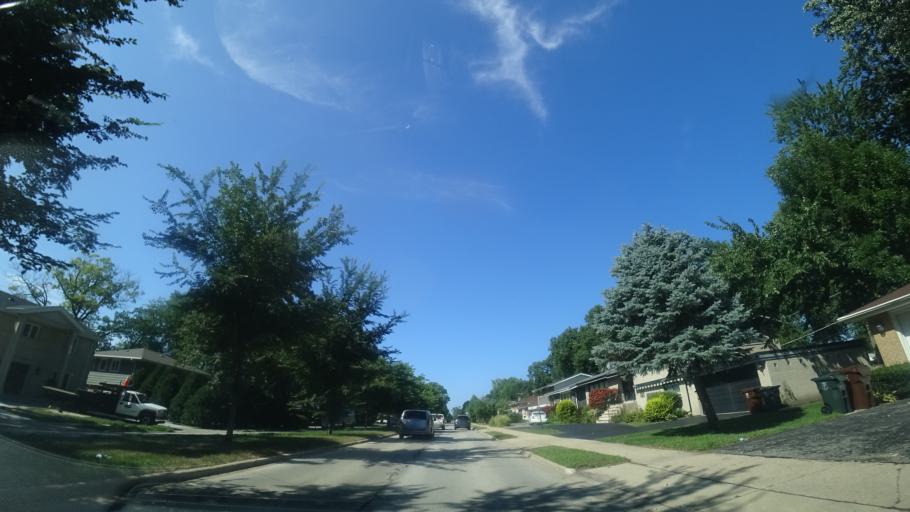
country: US
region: Illinois
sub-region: Cook County
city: Skokie
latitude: 42.0437
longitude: -87.7276
